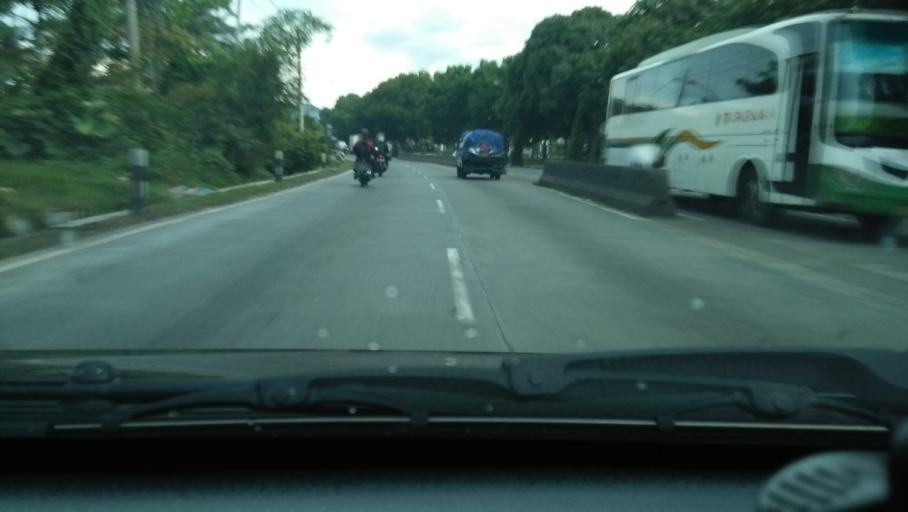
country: ID
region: Central Java
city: Ungaran
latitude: -7.0908
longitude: 110.4089
